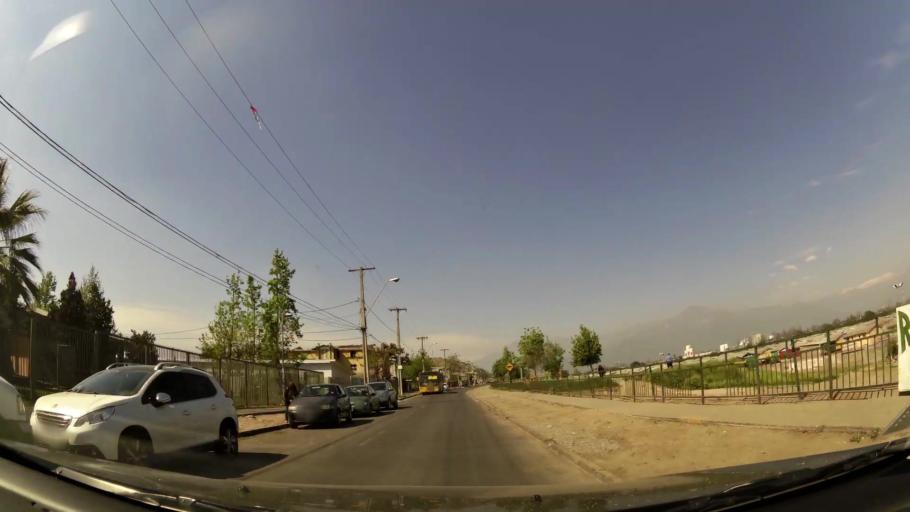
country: CL
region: Santiago Metropolitan
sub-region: Provincia de Cordillera
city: Puente Alto
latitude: -33.6282
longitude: -70.6162
